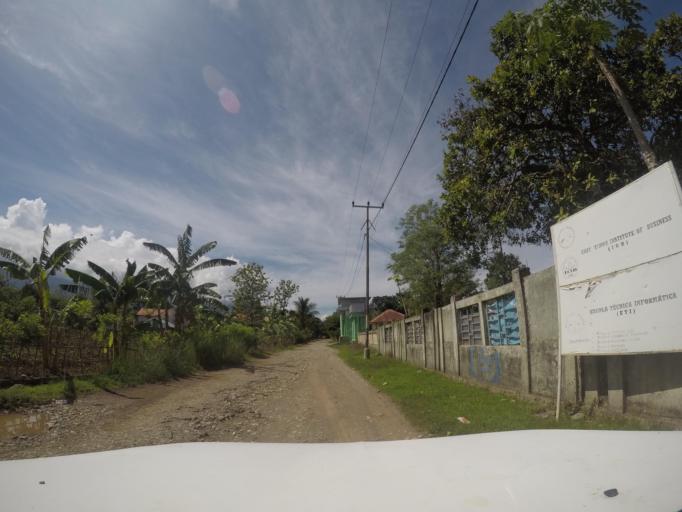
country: TL
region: Bobonaro
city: Maliana
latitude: -8.9896
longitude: 125.1990
